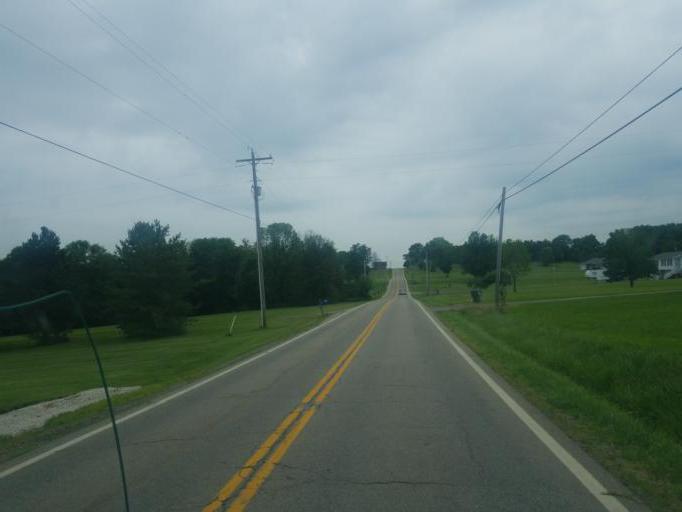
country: US
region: Ohio
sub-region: Carroll County
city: Carrollton
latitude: 40.6356
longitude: -81.0654
